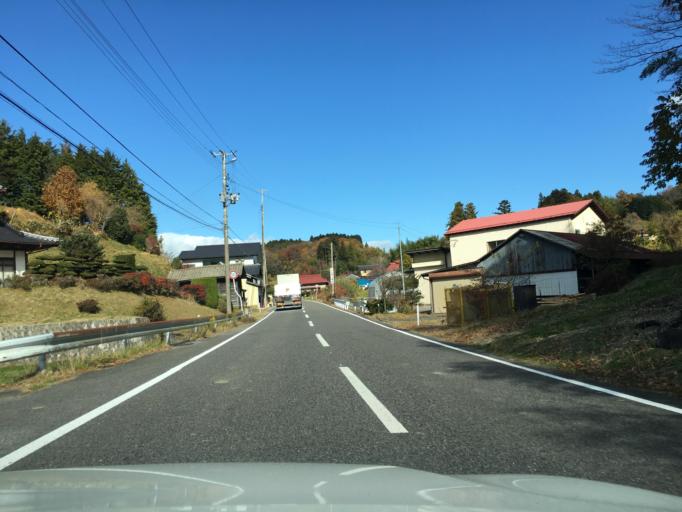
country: JP
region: Fukushima
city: Miharu
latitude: 37.4690
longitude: 140.4926
